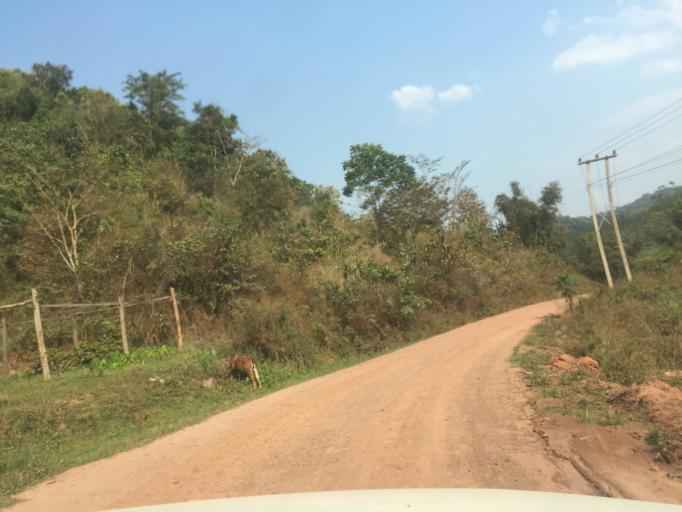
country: LA
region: Oudomxai
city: Muang La
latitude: 21.0746
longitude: 101.8203
